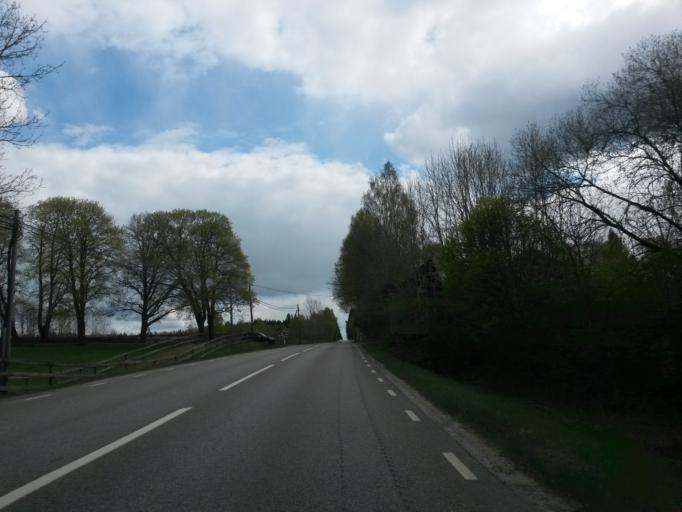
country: SE
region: Vaestra Goetaland
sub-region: Vargarda Kommun
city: Vargarda
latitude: 57.9400
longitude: 12.8489
